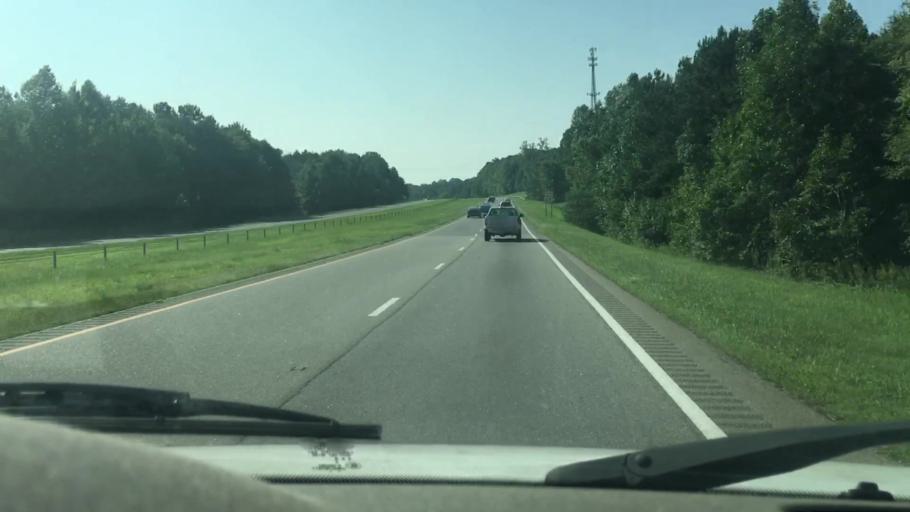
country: US
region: North Carolina
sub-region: Lincoln County
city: Lowesville
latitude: 35.3734
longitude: -80.9963
